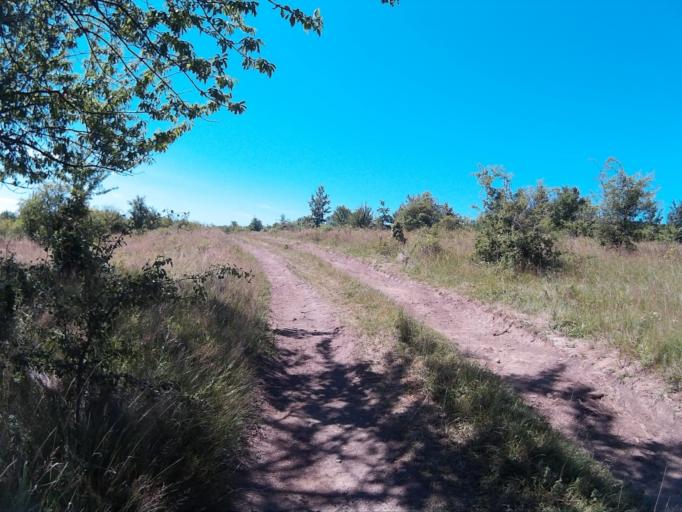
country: HU
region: Veszprem
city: Urkut
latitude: 47.1345
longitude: 17.6546
